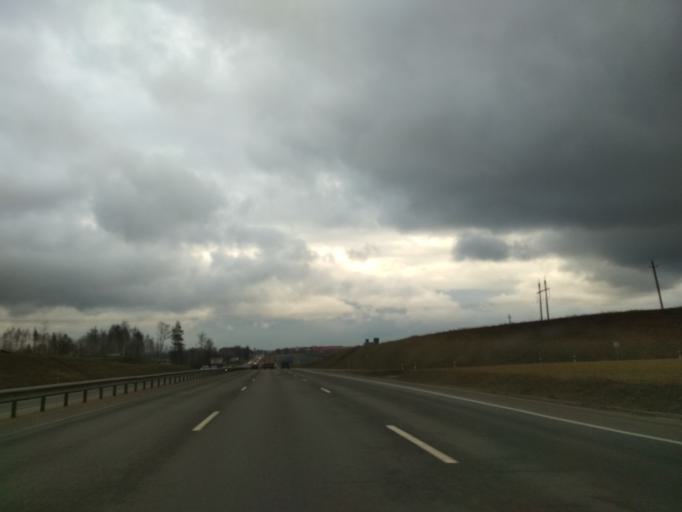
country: BY
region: Minsk
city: Pryvol'ny
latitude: 53.8135
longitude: 27.7755
